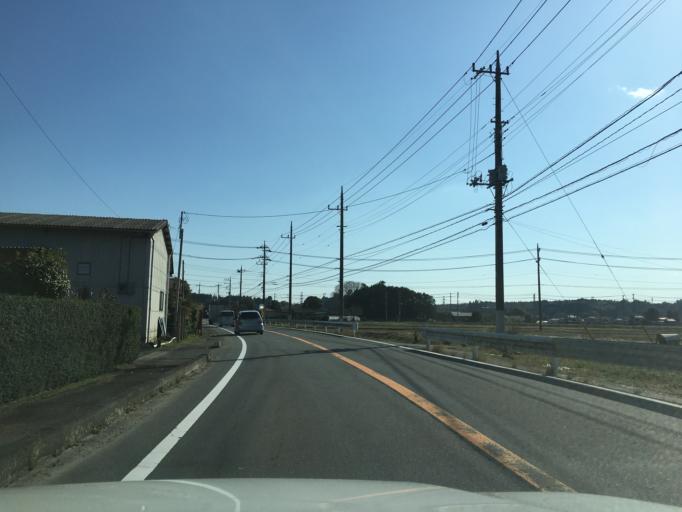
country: JP
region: Ibaraki
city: Omiya
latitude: 36.4991
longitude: 140.3717
